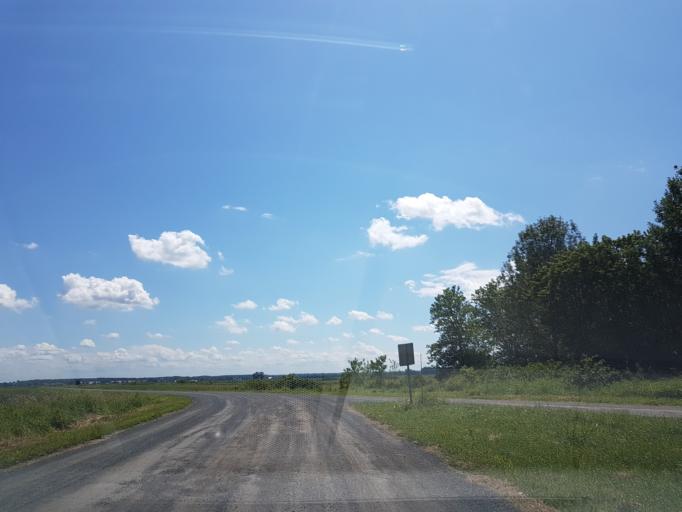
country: CA
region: Quebec
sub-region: Mauricie
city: Pierreville
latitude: 46.1586
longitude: -72.7553
